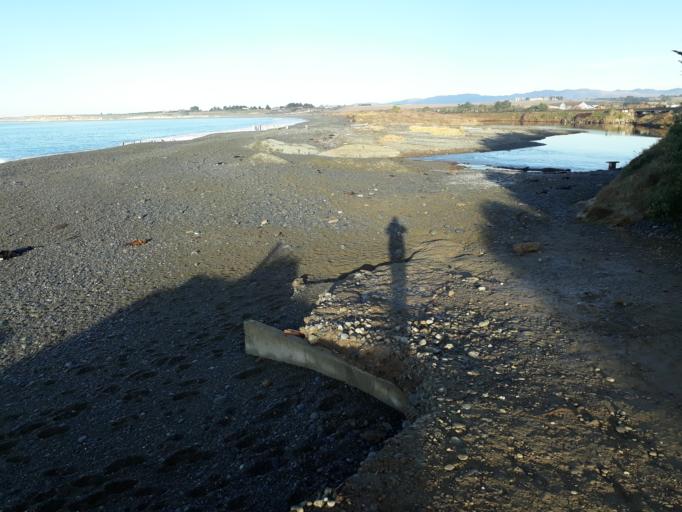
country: NZ
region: Canterbury
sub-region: Timaru District
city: Timaru
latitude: -44.4158
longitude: 171.2637
